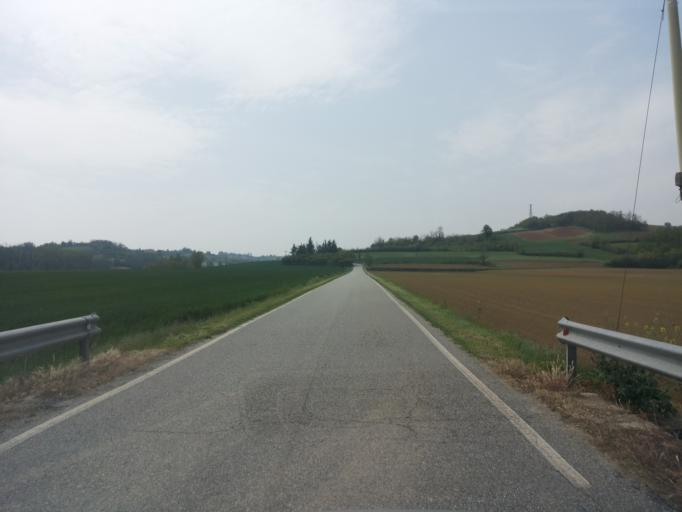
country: IT
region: Piedmont
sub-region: Provincia di Alessandria
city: Mirabello Monferrato
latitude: 45.0213
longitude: 8.5149
